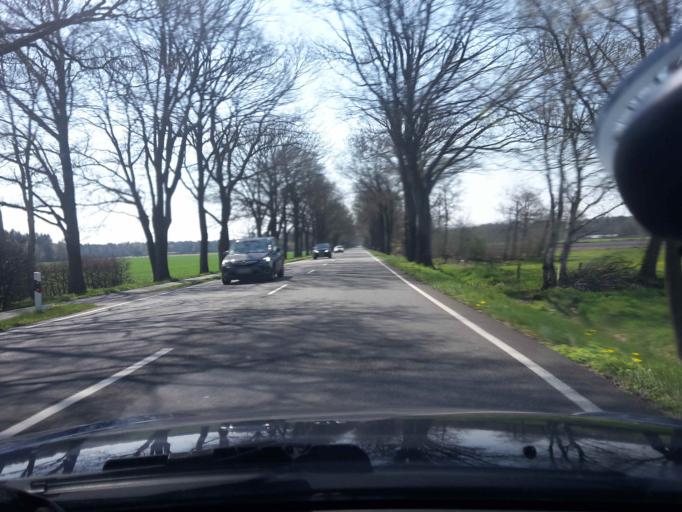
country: DE
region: Lower Saxony
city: Handeloh
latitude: 53.1757
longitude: 9.8403
